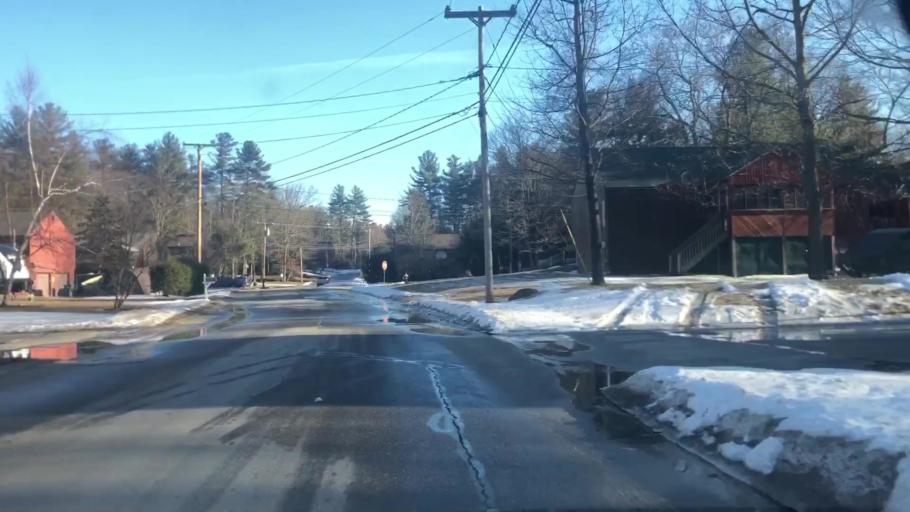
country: US
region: New Hampshire
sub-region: Hillsborough County
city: Milford
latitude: 42.8354
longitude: -71.6802
